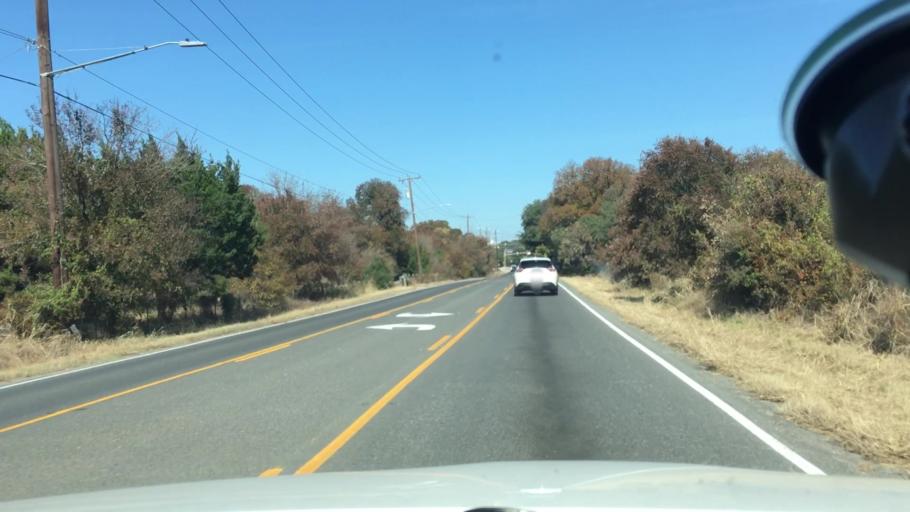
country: US
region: Texas
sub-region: Bexar County
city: Hollywood Park
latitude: 29.5900
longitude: -98.4238
